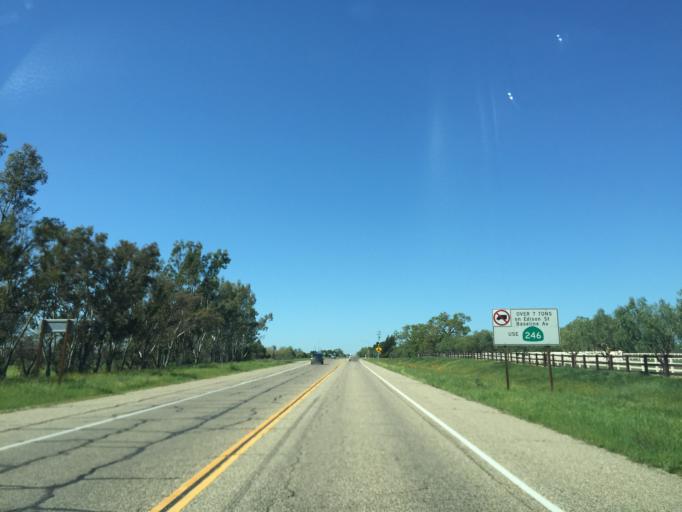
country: US
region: California
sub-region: Santa Barbara County
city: Santa Ynez
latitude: 34.6313
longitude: -120.0790
